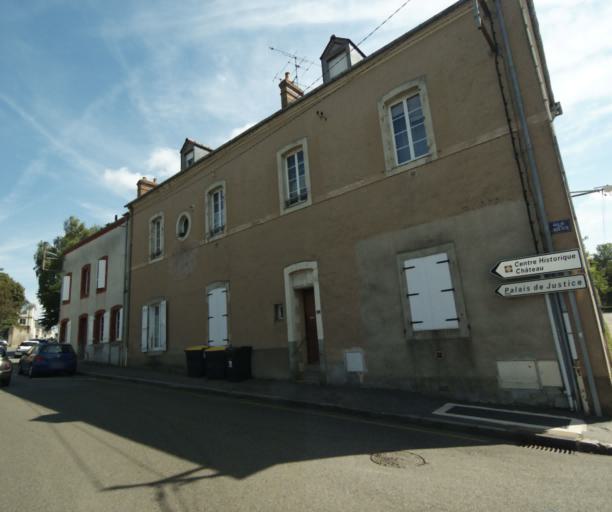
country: FR
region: Pays de la Loire
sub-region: Departement de la Mayenne
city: Laval
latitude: 48.0647
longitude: -0.7753
